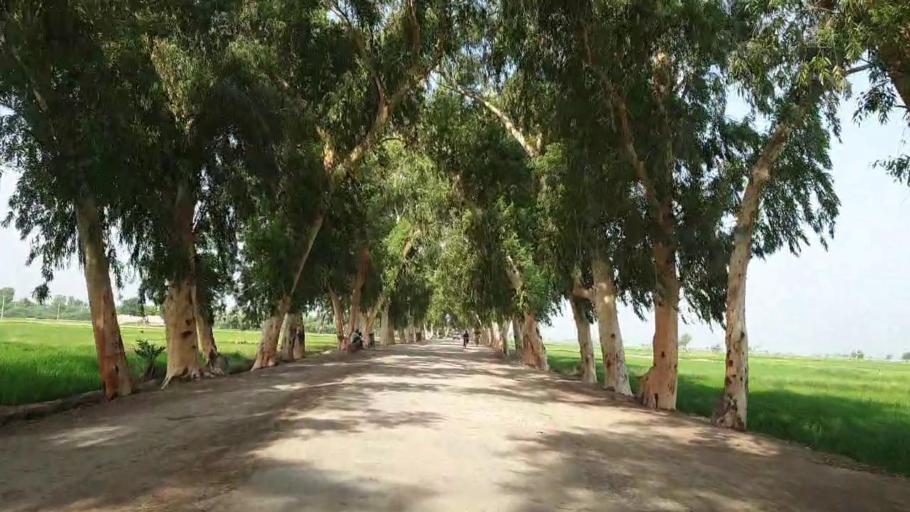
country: PK
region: Sindh
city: Lakhi
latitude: 27.8160
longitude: 68.7352
